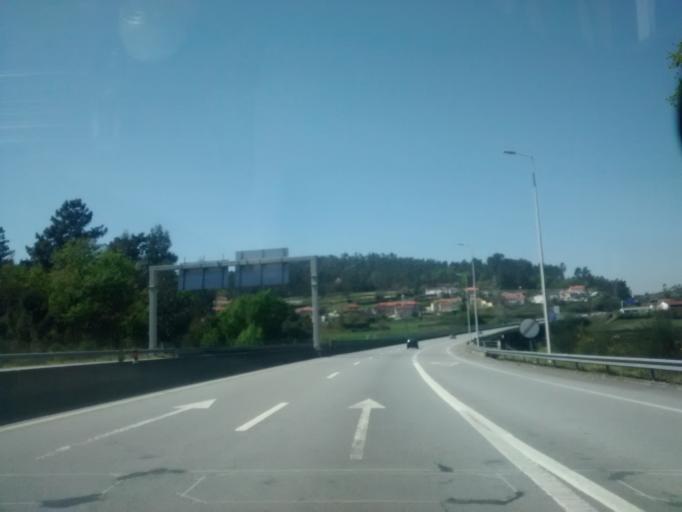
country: PT
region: Braga
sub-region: Braga
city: Braga
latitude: 41.5172
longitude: -8.4302
